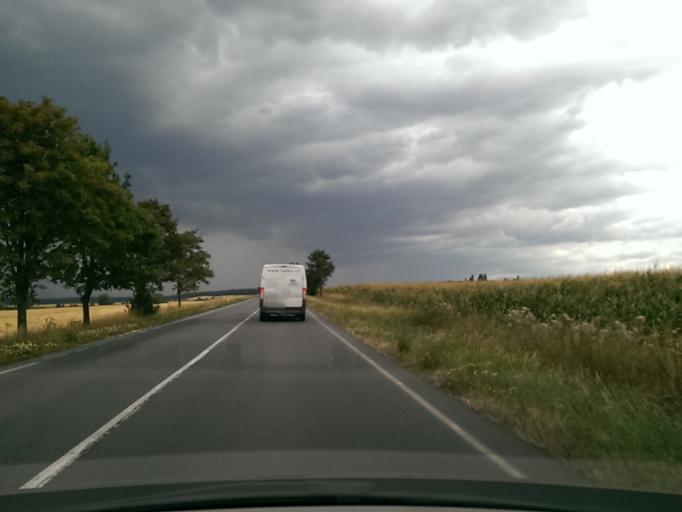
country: CZ
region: Central Bohemia
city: Loucen
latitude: 50.2458
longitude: 15.0087
